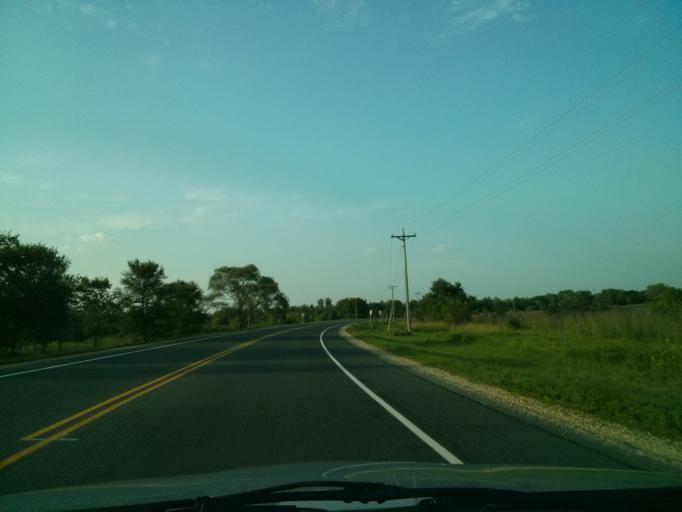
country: US
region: Wisconsin
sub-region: Saint Croix County
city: North Hudson
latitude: 45.0147
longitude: -92.6752
